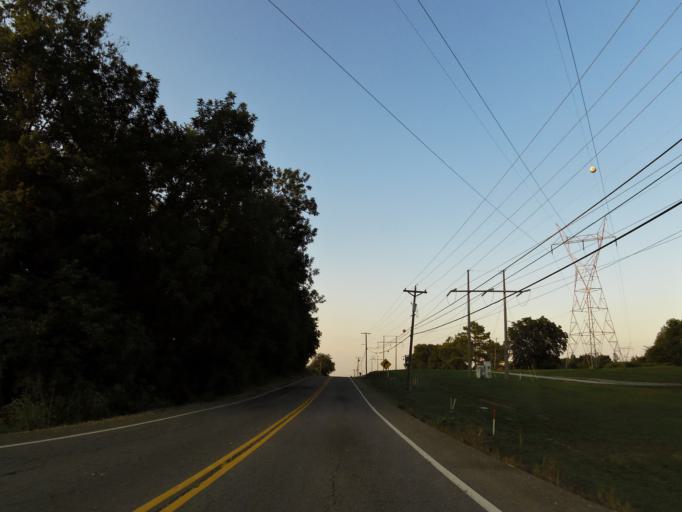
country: US
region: Tennessee
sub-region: Loudon County
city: Loudon
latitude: 35.6896
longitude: -84.3884
